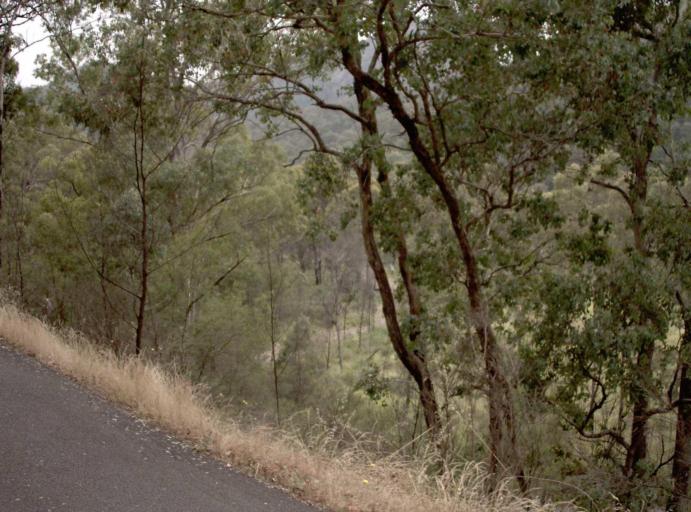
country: AU
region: Victoria
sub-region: Wellington
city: Heyfield
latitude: -37.7429
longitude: 146.6673
